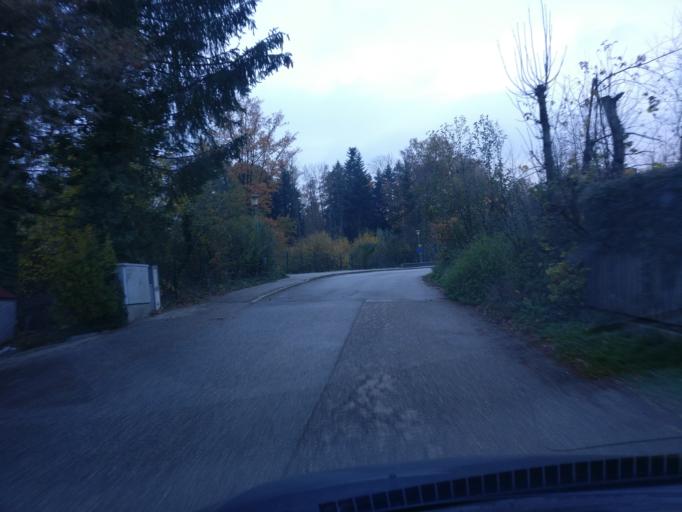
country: AT
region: Salzburg
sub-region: Politischer Bezirk Salzburg-Umgebung
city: Elixhausen
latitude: 47.8588
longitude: 13.0652
